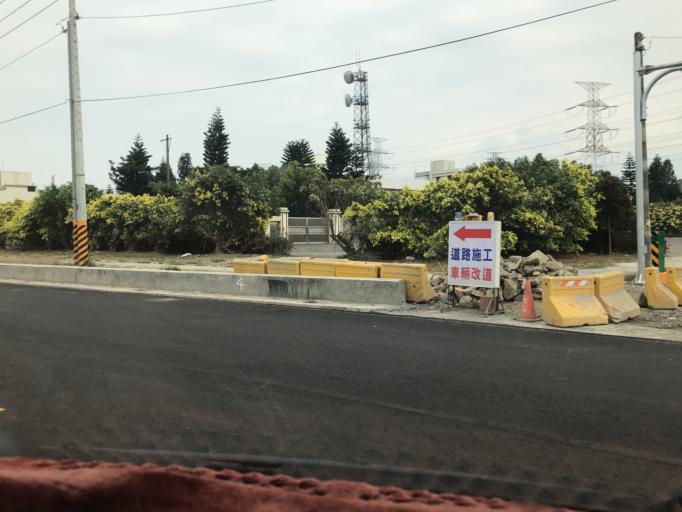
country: TW
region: Taiwan
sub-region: Pingtung
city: Pingtung
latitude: 22.4155
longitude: 120.6088
